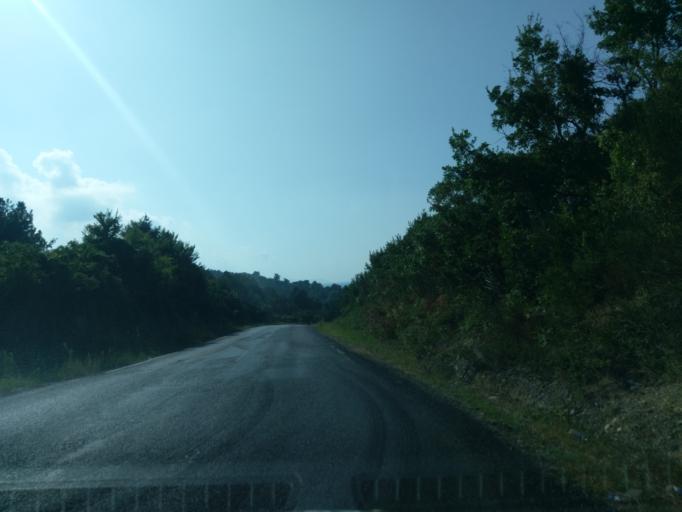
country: TR
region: Sinop
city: Yenikonak
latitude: 41.9427
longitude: 34.6997
